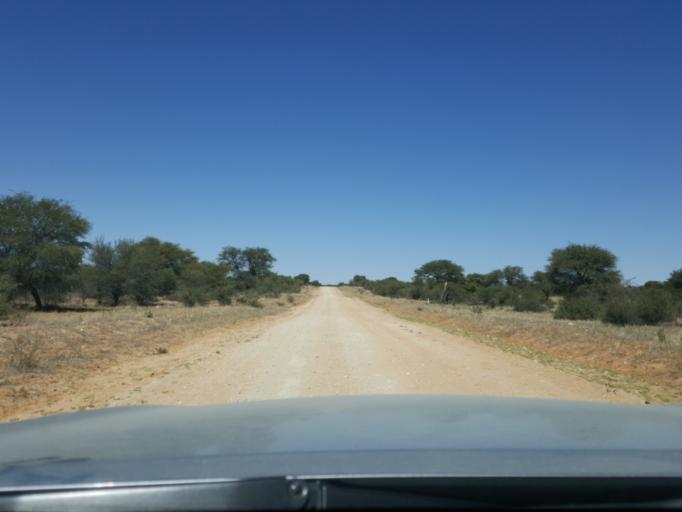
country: BW
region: Kgalagadi
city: Hukuntsi
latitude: -24.1099
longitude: 21.2335
